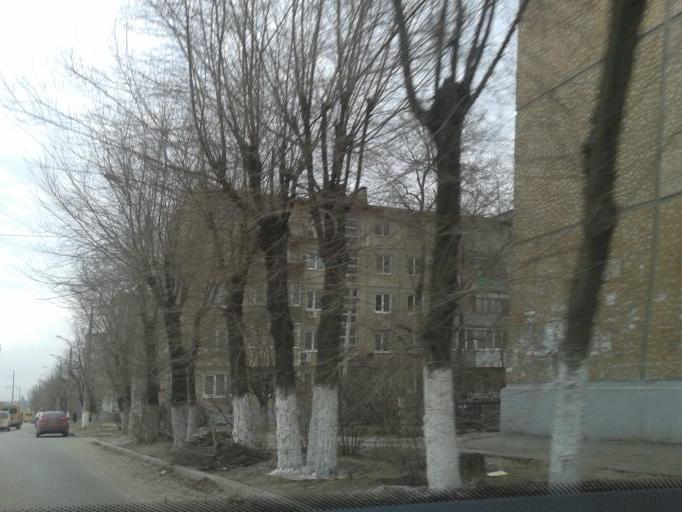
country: RU
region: Volgograd
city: Gorodishche
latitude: 48.7672
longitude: 44.4817
